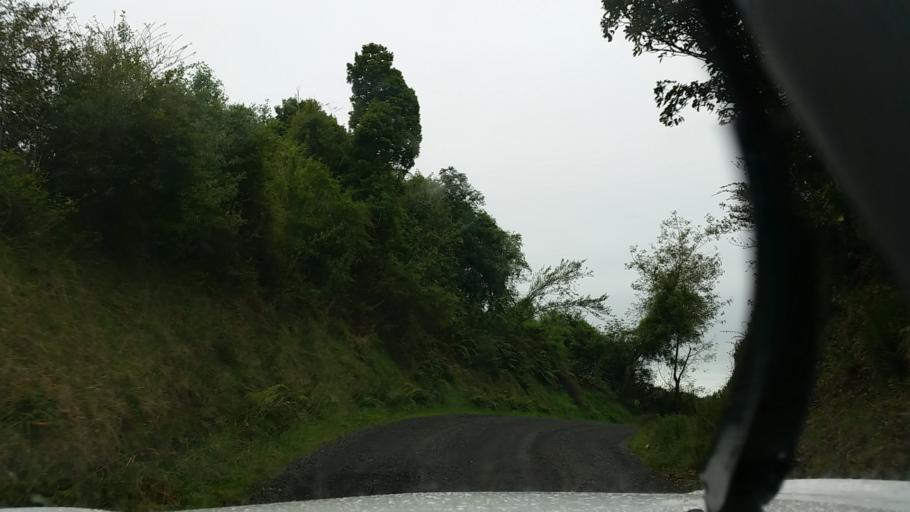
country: NZ
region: Bay of Plenty
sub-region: Rotorua District
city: Rotorua
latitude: -37.9836
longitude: 176.3974
